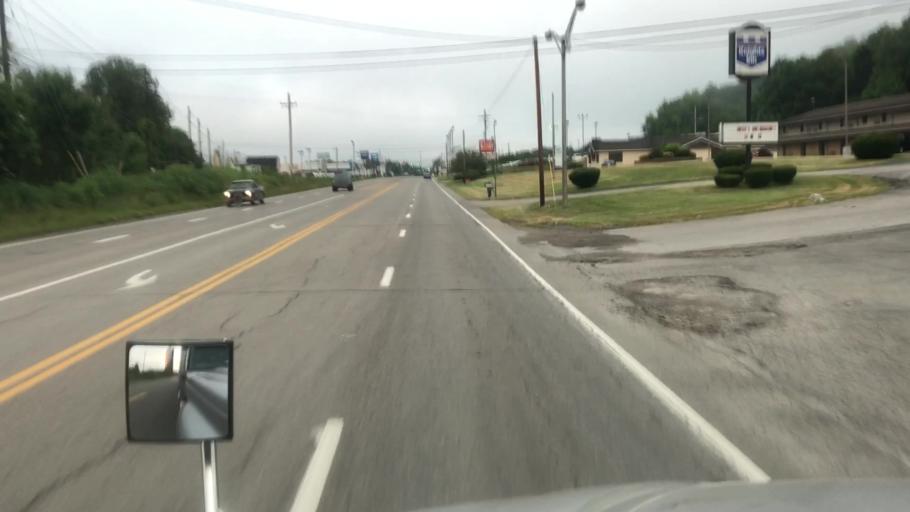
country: US
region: Pennsylvania
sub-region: Venango County
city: Franklin
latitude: 41.4082
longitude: -79.7954
